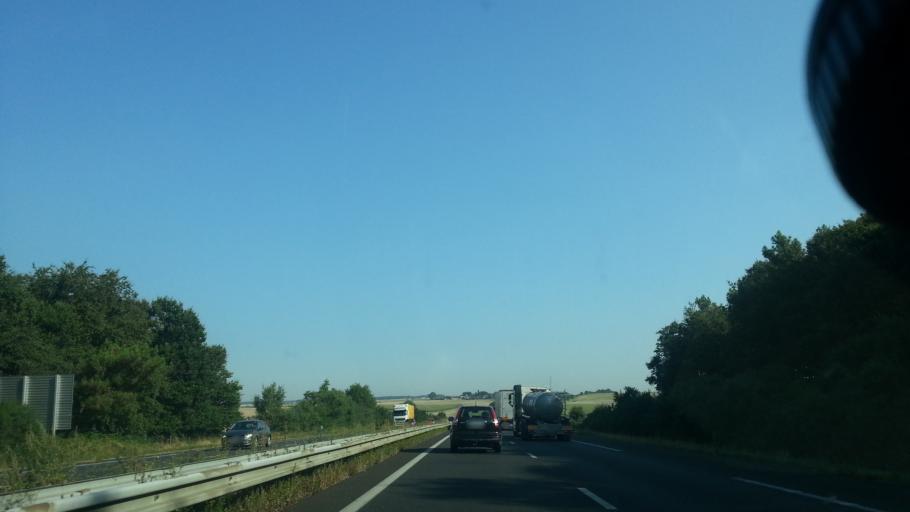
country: FR
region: Poitou-Charentes
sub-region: Departement de la Vienne
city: Les Ormes
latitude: 46.9683
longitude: 0.5475
